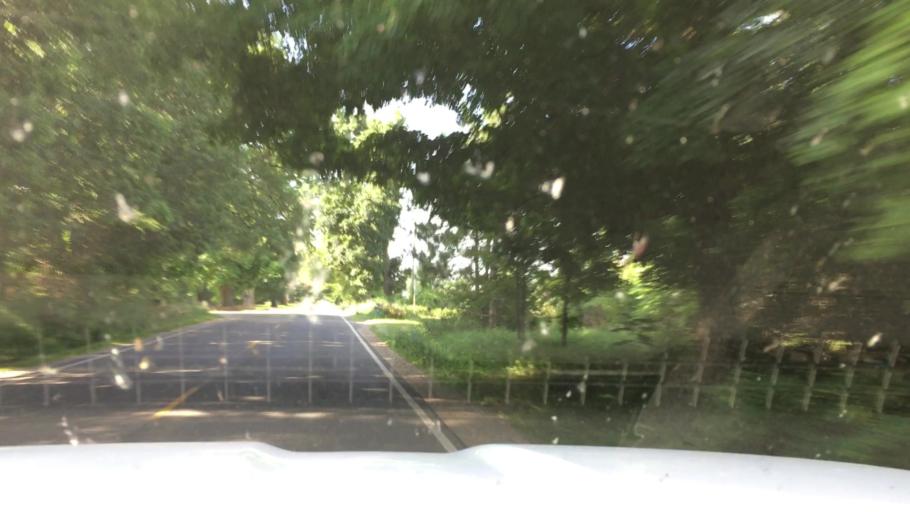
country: US
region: Michigan
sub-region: Barry County
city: Stony Point
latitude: 42.4359
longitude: -85.4545
